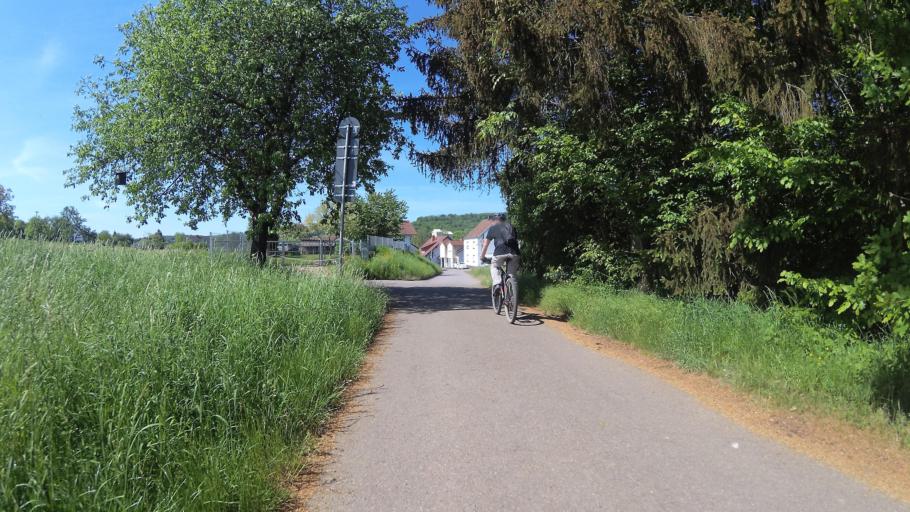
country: DE
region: Saarland
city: Gersheim
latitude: 49.1887
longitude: 7.1673
